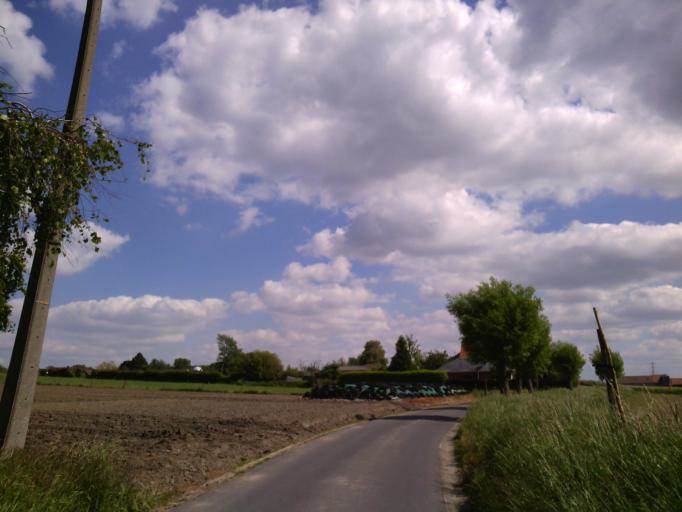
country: BE
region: Flanders
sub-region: Provincie West-Vlaanderen
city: Wevelgem
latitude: 50.7894
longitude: 3.1735
